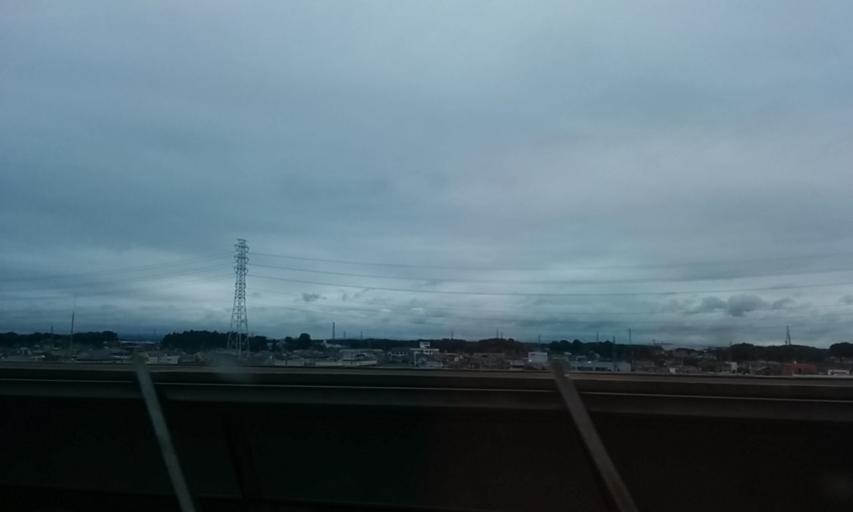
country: JP
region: Tochigi
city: Mibu
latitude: 36.3739
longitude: 139.8416
